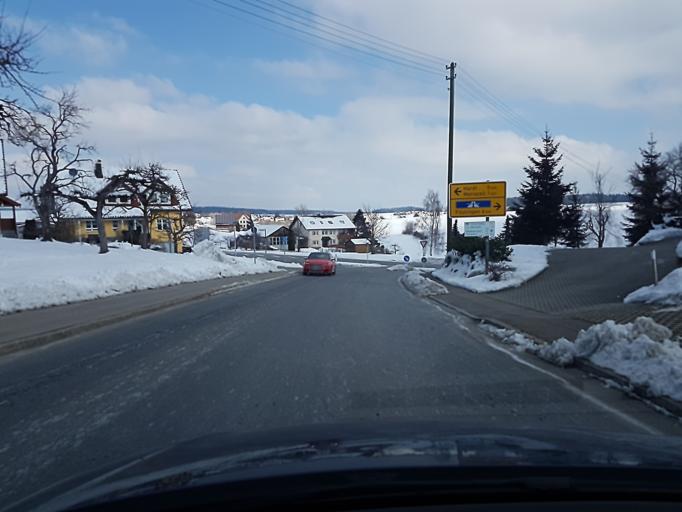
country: DE
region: Baden-Wuerttemberg
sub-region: Freiburg Region
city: Hardt
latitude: 48.1734
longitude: 8.4602
